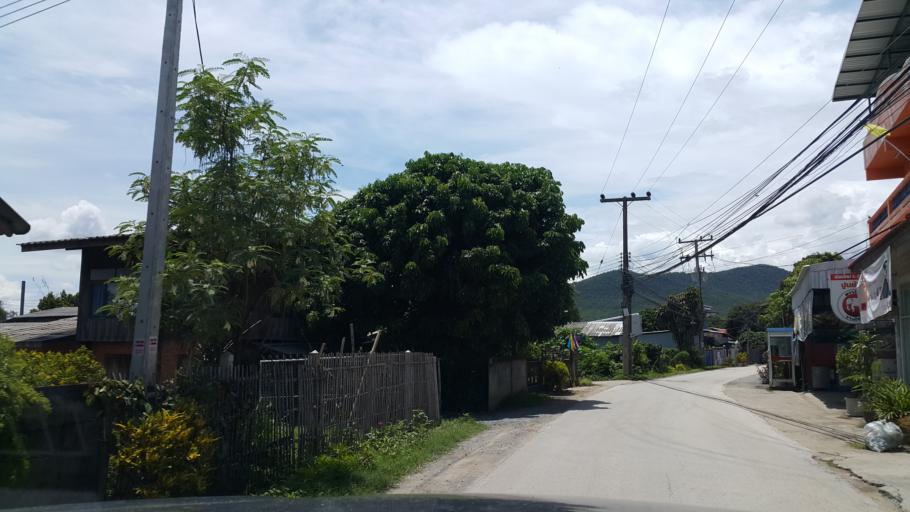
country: TH
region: Chiang Mai
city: Mae On
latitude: 18.7281
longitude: 99.2078
